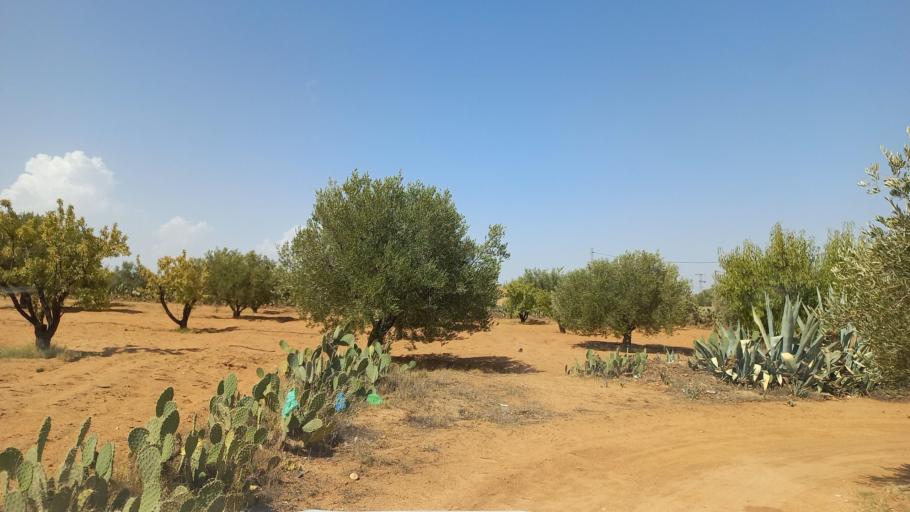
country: TN
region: Al Qasrayn
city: Kasserine
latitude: 35.2241
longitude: 9.0427
